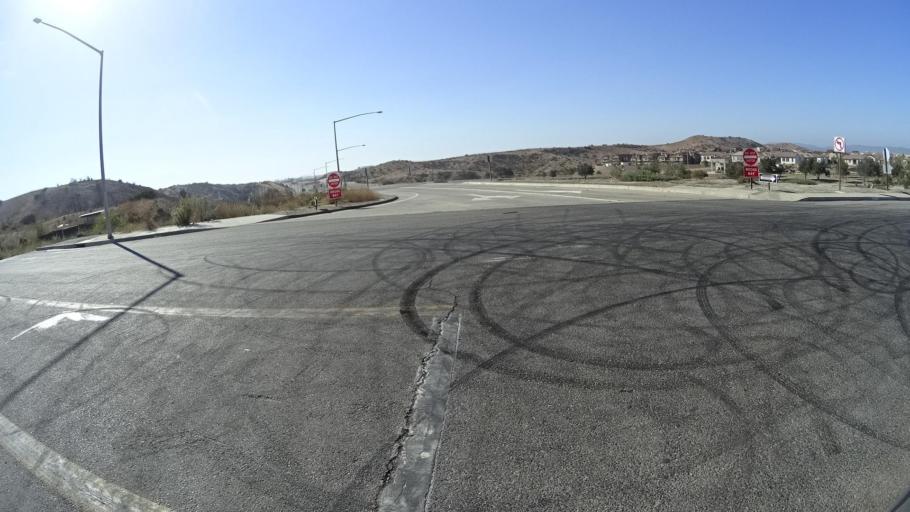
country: US
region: California
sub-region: Orange County
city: Foothill Ranch
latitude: 33.6960
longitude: -117.6913
